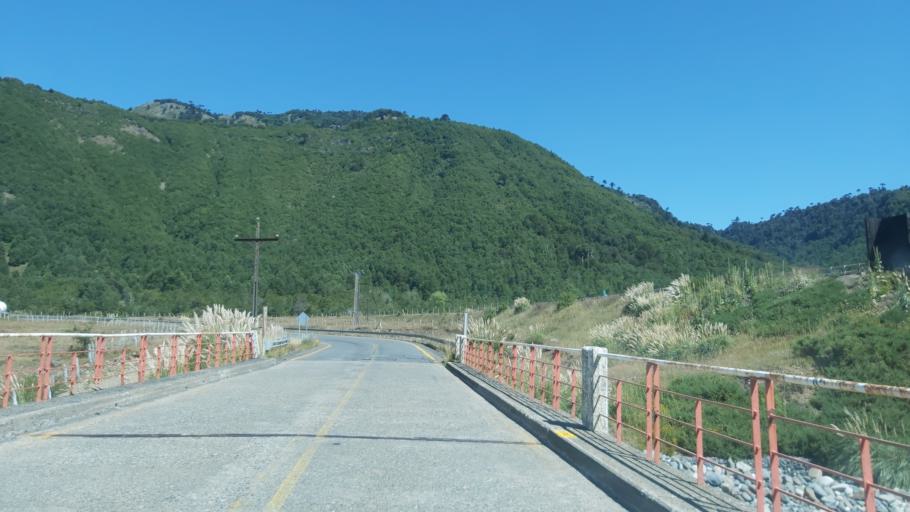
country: CL
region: Araucania
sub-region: Provincia de Cautin
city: Vilcun
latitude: -38.5663
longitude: -71.4927
